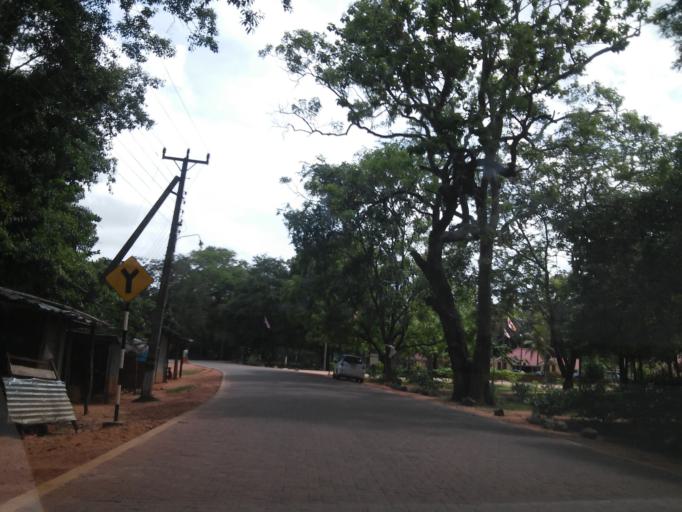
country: LK
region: North Central
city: Anuradhapura
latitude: 8.3695
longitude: 80.3958
